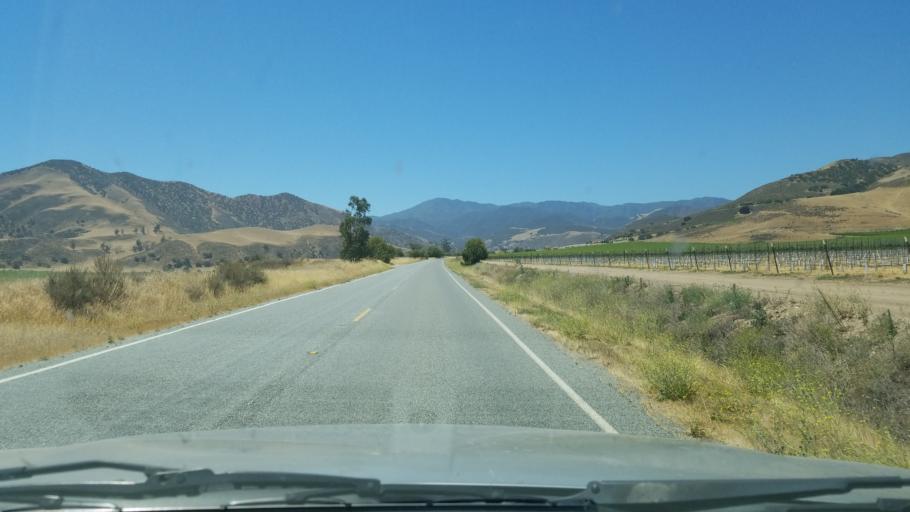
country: US
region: California
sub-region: Monterey County
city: Greenfield
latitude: 36.2959
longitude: -121.3141
